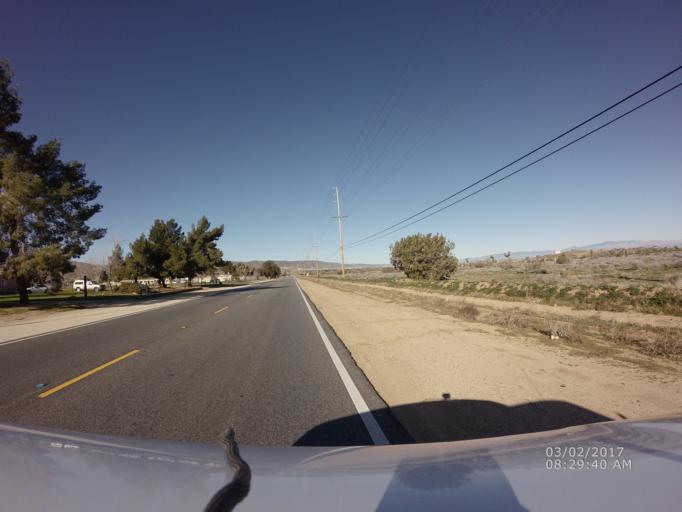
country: US
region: California
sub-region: Los Angeles County
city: Quartz Hill
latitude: 34.6311
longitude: -118.1870
